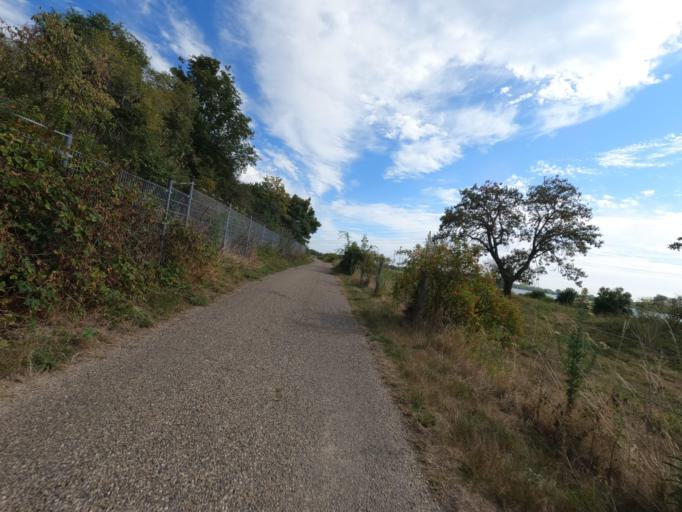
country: NL
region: Limburg
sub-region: Gemeente Maasgouw
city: Maasbracht
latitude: 51.1638
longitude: 5.8909
